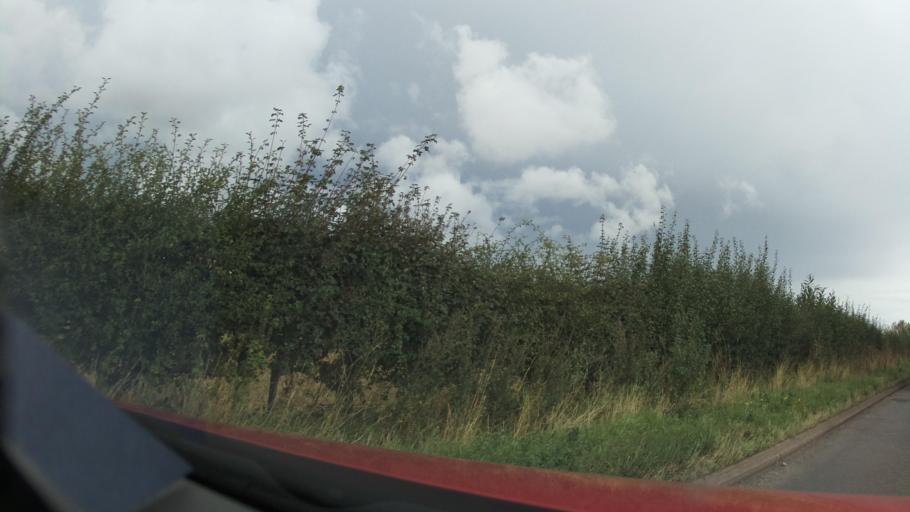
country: GB
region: England
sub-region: Shropshire
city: Woodcote
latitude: 52.7346
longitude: -2.3372
